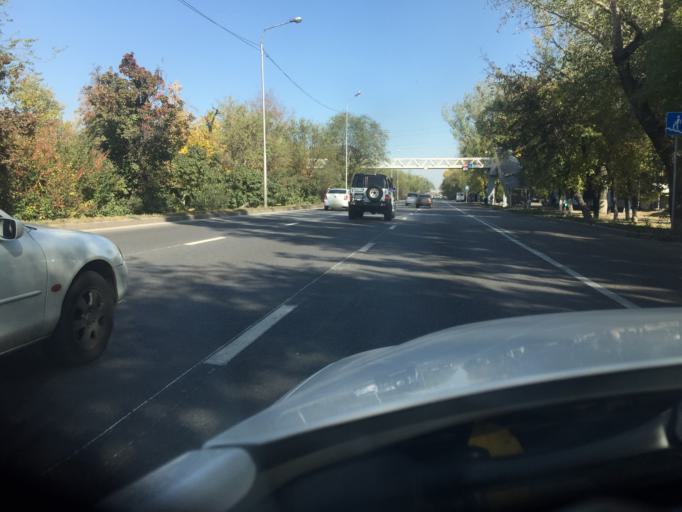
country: KZ
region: Almaty Qalasy
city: Almaty
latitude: 43.2615
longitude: 76.8945
